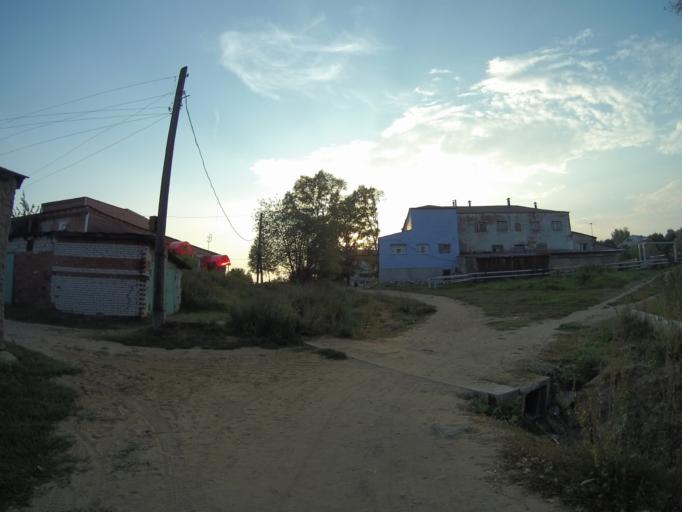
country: RU
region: Vladimir
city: Orgtrud
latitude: 56.1821
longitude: 40.6079
